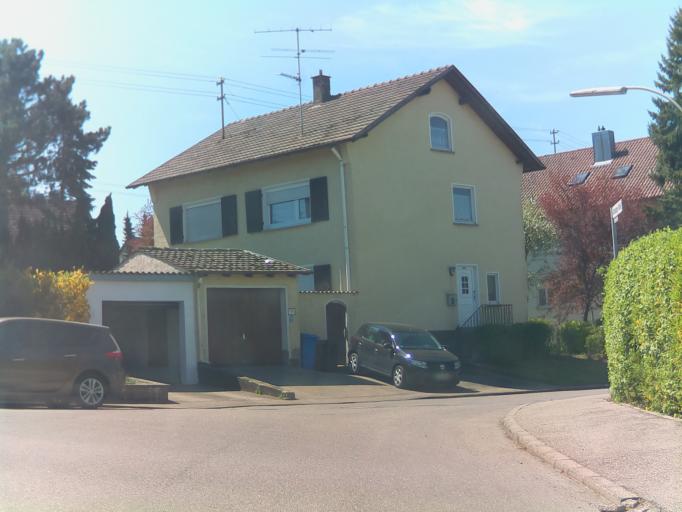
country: DE
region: Baden-Wuerttemberg
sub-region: Freiburg Region
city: Zimmern ob Rottweil
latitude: 48.1672
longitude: 8.6010
